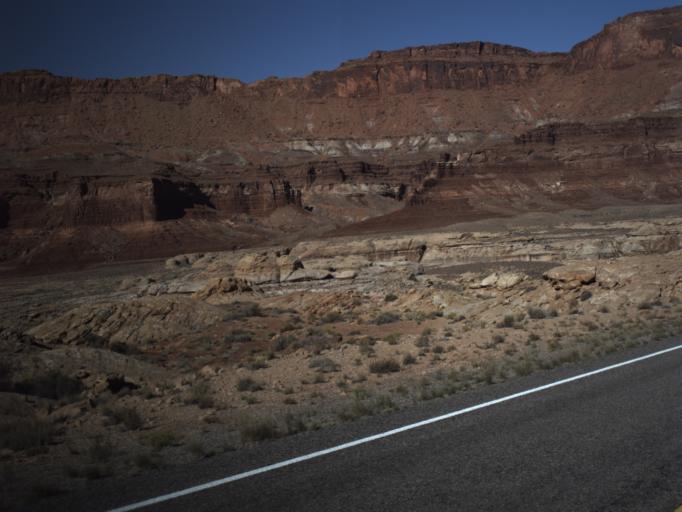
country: US
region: Utah
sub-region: San Juan County
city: Blanding
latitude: 37.9099
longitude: -110.3850
